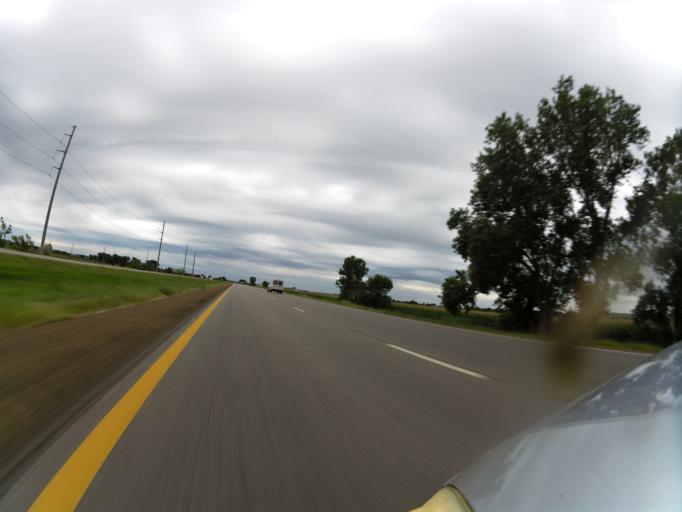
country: US
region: Kansas
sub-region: Sedgwick County
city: Maize
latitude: 37.7771
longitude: -97.4579
